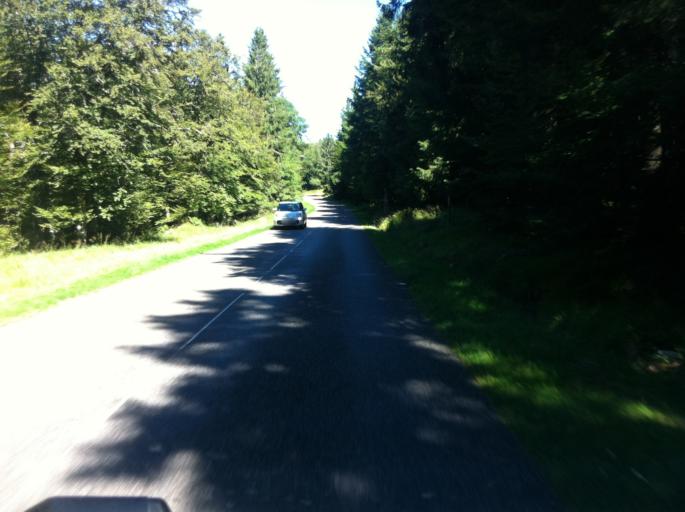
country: FR
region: Alsace
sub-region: Departement du Haut-Rhin
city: Soultzeren
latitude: 48.1258
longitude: 7.0732
